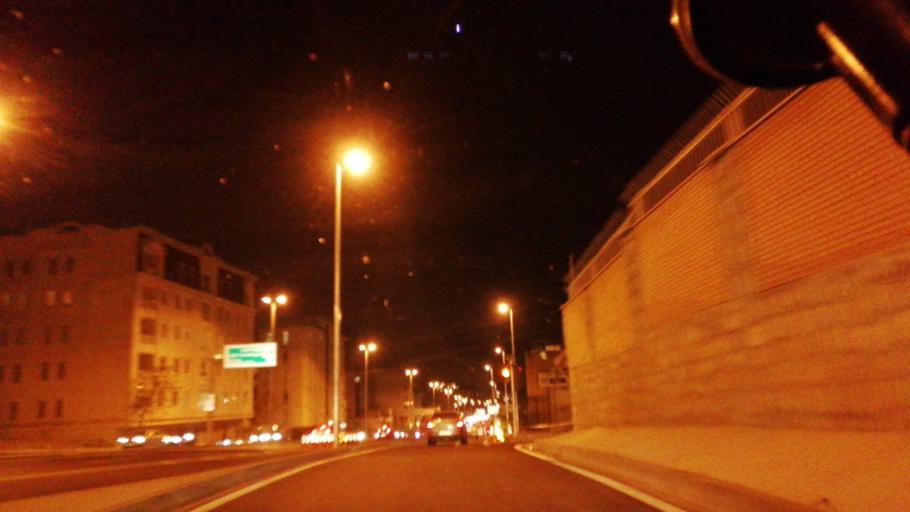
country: IR
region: Tehran
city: Tajrish
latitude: 35.7955
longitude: 51.4894
